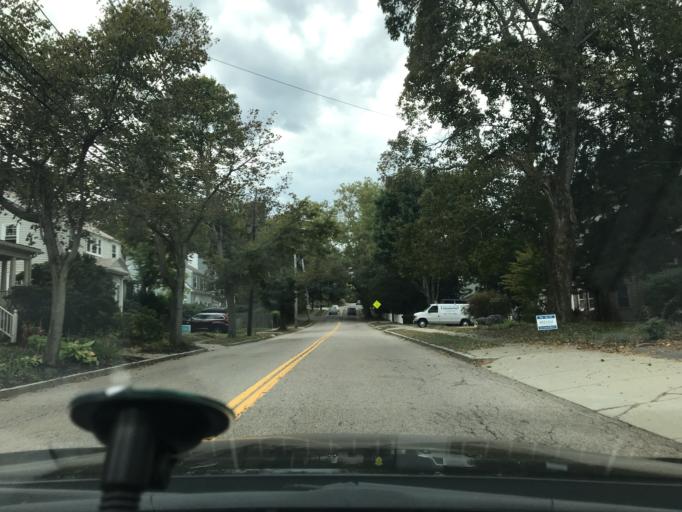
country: US
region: Massachusetts
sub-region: Middlesex County
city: Watertown
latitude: 42.3509
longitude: -71.1800
